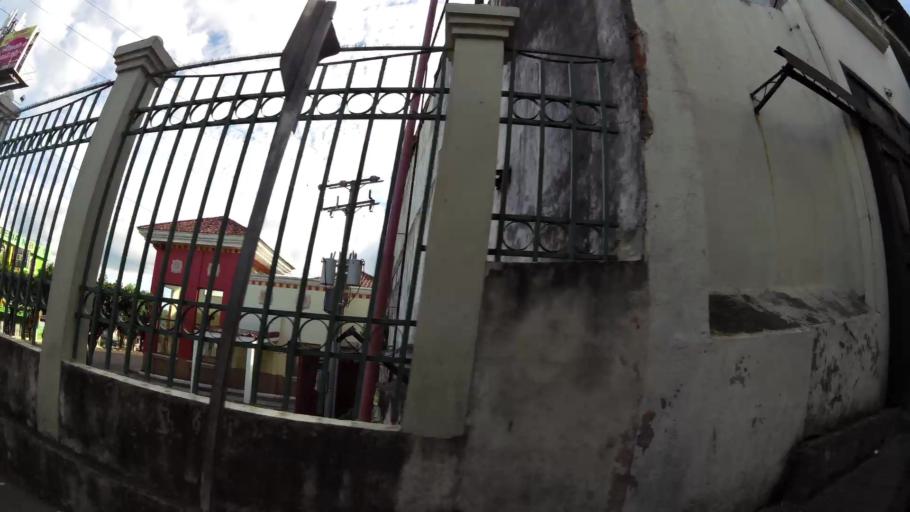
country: SV
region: Cuscatlan
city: Cojutepeque
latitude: 13.7220
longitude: -88.9339
